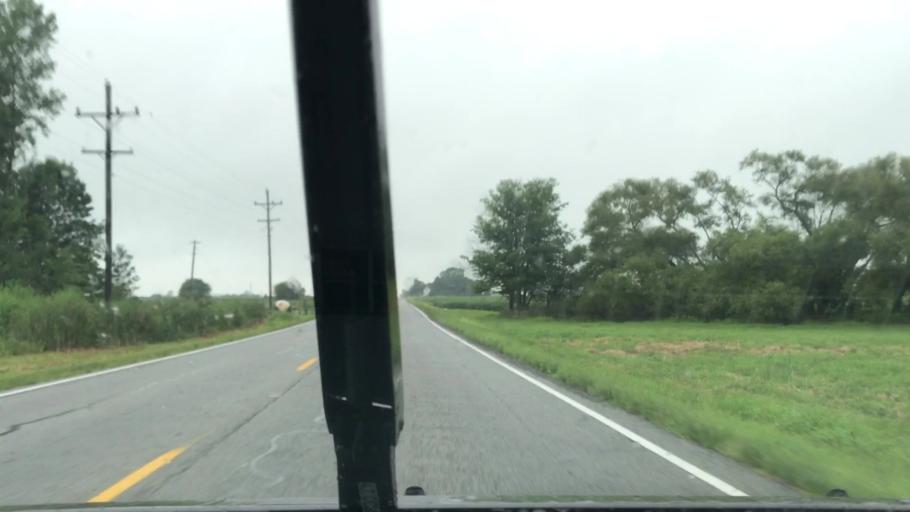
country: US
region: Indiana
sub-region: Hamilton County
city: Sheridan
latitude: 40.1287
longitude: -86.2935
